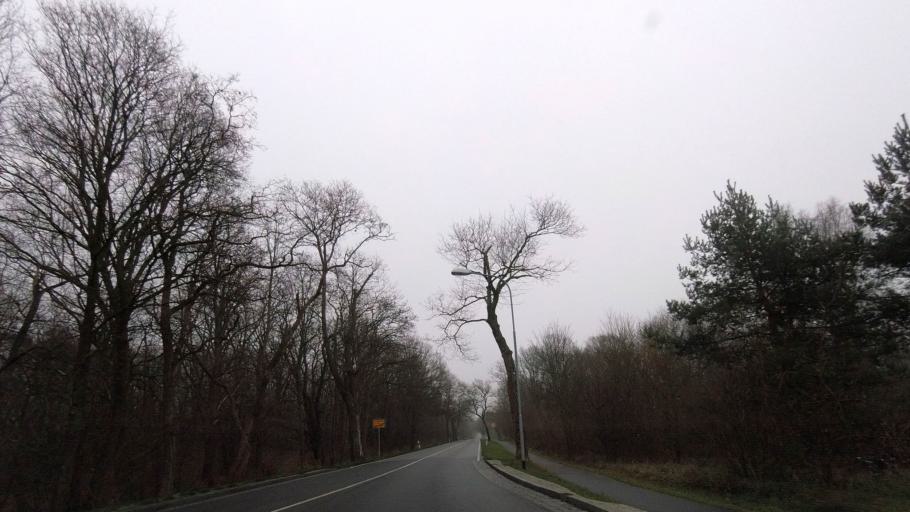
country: DE
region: Brandenburg
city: Niedergorsdorf
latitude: 52.0082
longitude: 13.0123
